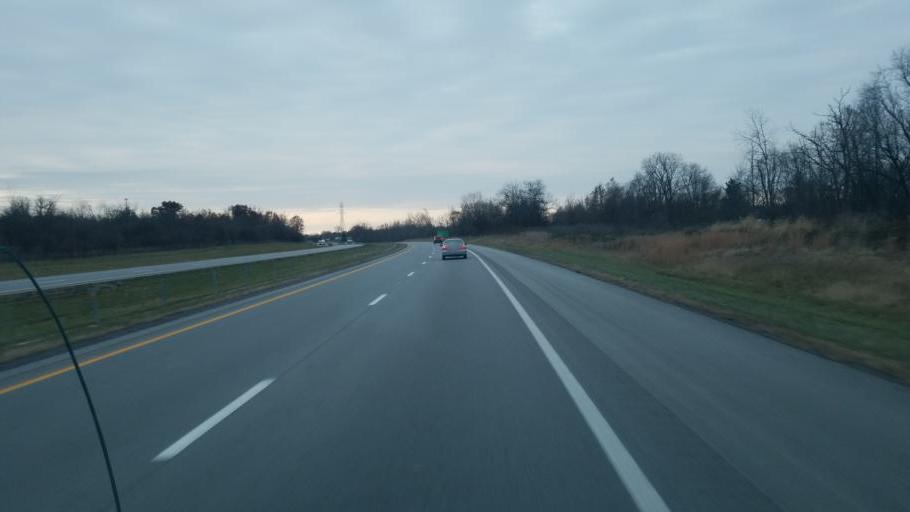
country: US
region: Ohio
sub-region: Allen County
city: Fort Shawnee
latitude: 40.6777
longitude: -84.1302
